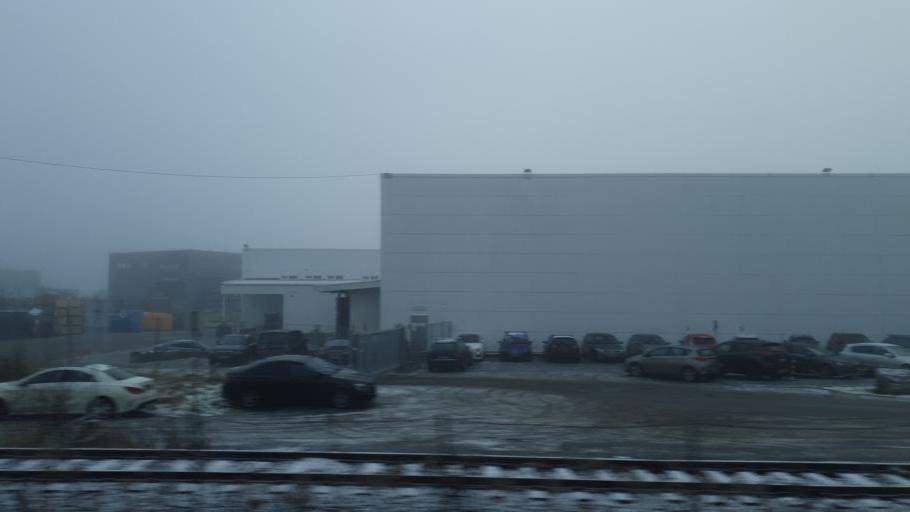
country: NO
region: Buskerud
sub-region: Lier
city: Lierbyen
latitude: 59.7519
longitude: 10.2626
